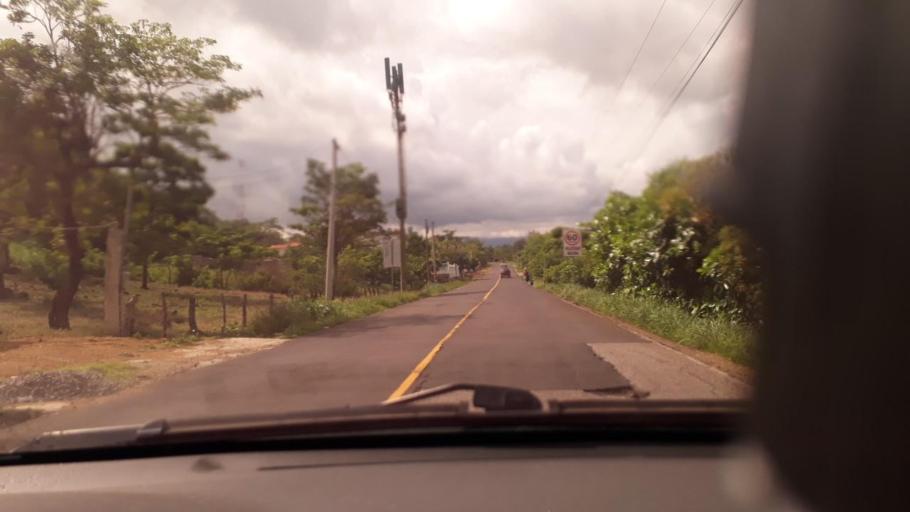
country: GT
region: Jutiapa
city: Quesada
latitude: 14.2150
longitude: -90.0243
